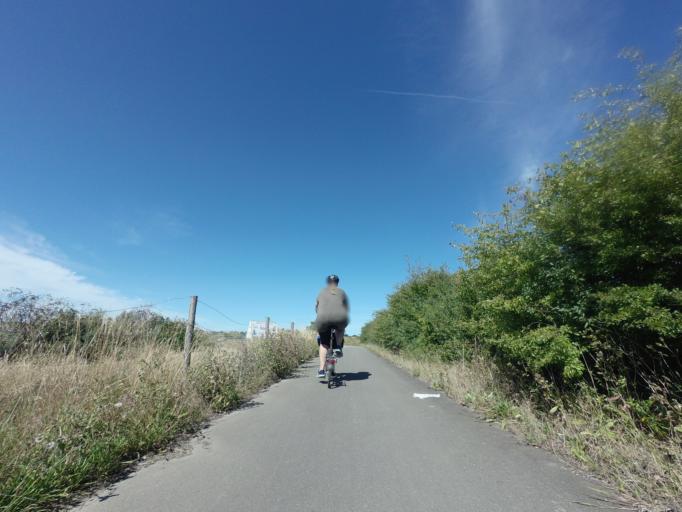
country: GB
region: England
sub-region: Kent
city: Sandwich
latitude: 51.3230
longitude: 1.3475
